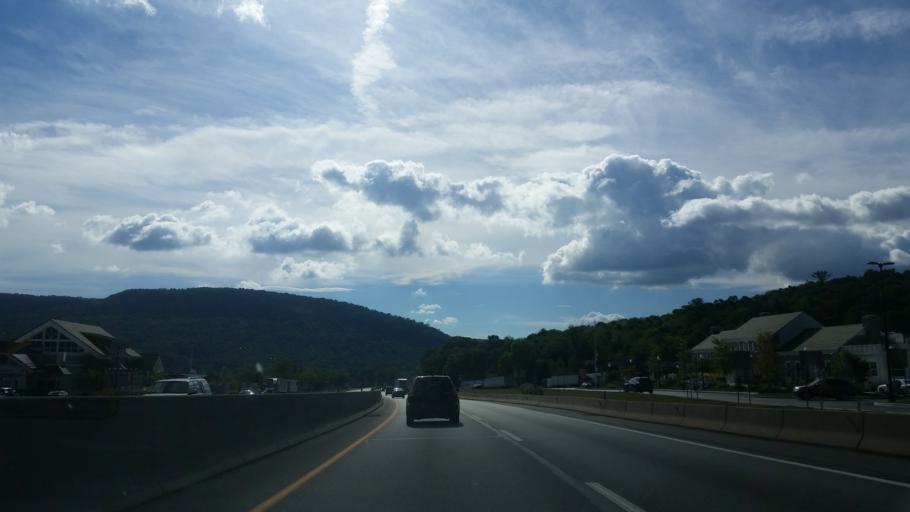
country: US
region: Pennsylvania
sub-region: Bedford County
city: Bedford
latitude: 40.0310
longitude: -78.4937
